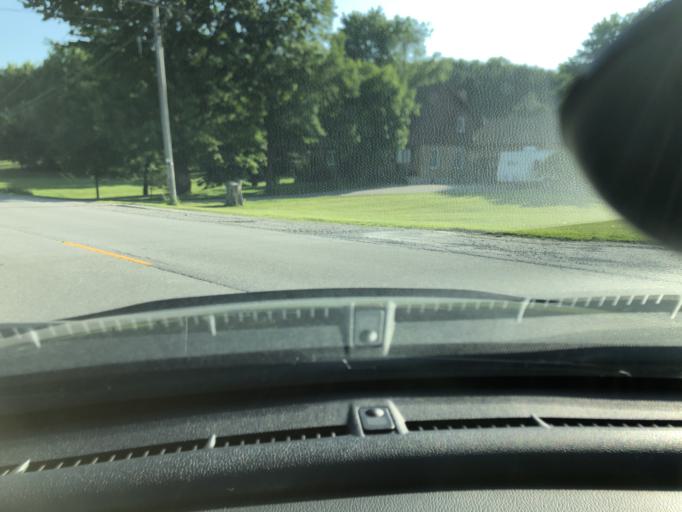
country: CA
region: Ontario
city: Stratford
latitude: 43.3879
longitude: -80.8373
